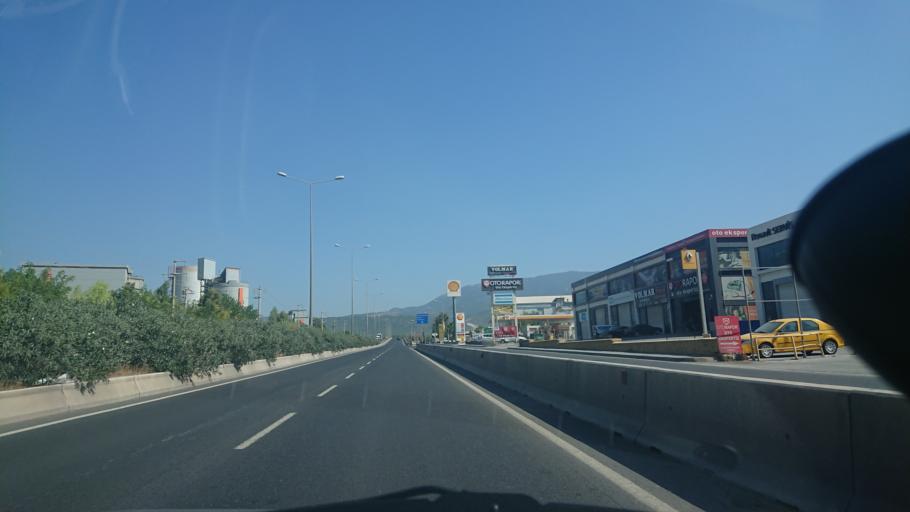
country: TR
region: Izmir
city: Bornova
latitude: 38.4545
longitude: 27.2600
